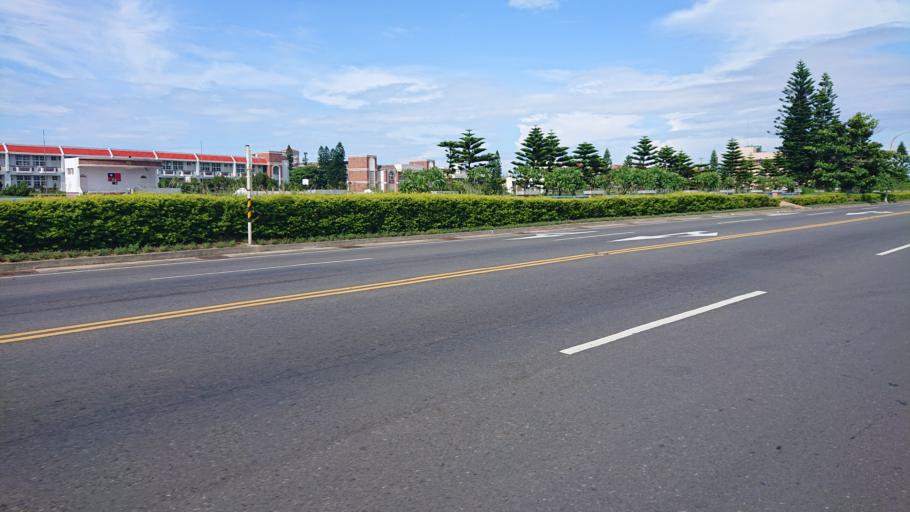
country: TW
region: Taiwan
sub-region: Penghu
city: Ma-kung
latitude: 23.5593
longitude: 119.5986
